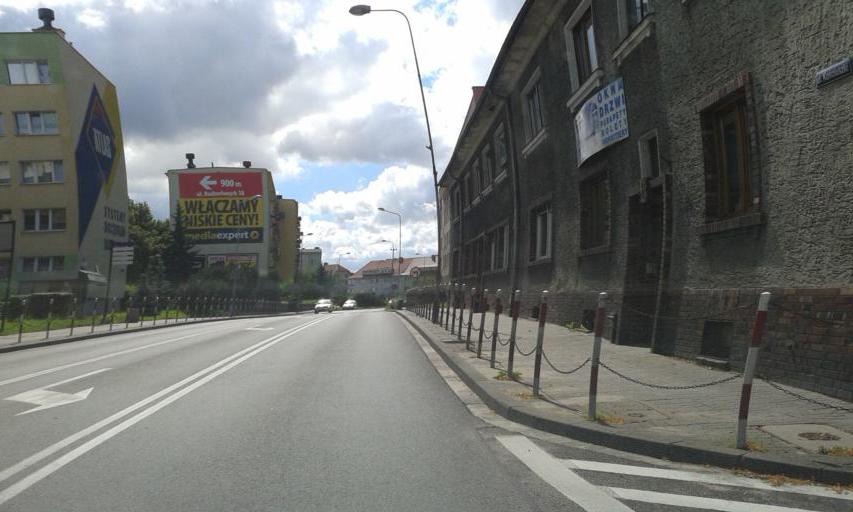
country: PL
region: West Pomeranian Voivodeship
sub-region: Powiat walecki
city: Walcz
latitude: 53.2755
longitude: 16.4742
